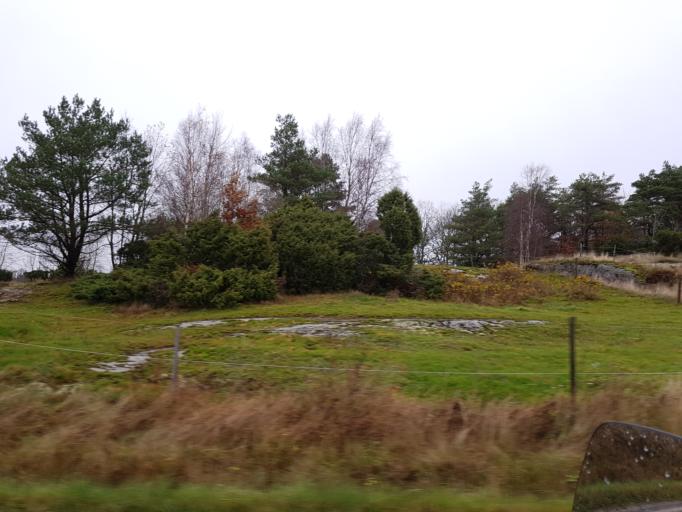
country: SE
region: Vaestra Goetaland
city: Svanesund
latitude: 58.1614
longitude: 11.7701
